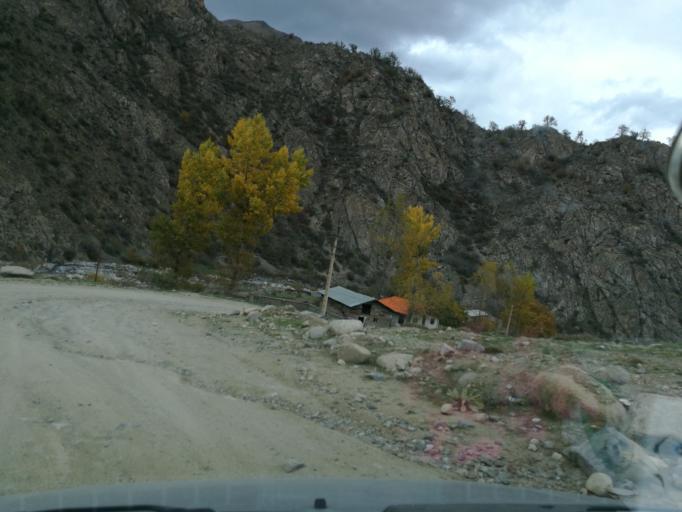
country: IR
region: Mazandaran
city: `Abbasabad
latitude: 36.4374
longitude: 51.0601
